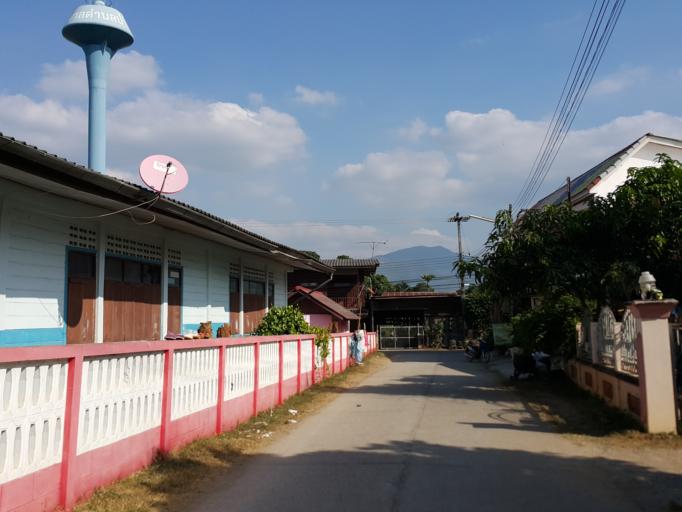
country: TH
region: Lamphun
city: Ban Hong
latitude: 18.2958
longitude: 98.8166
